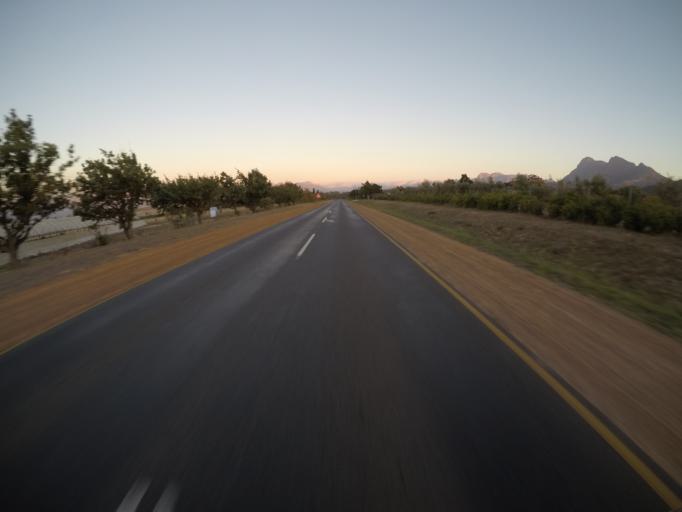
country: ZA
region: Western Cape
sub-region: Cape Winelands District Municipality
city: Paarl
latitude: -33.8046
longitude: 18.8947
